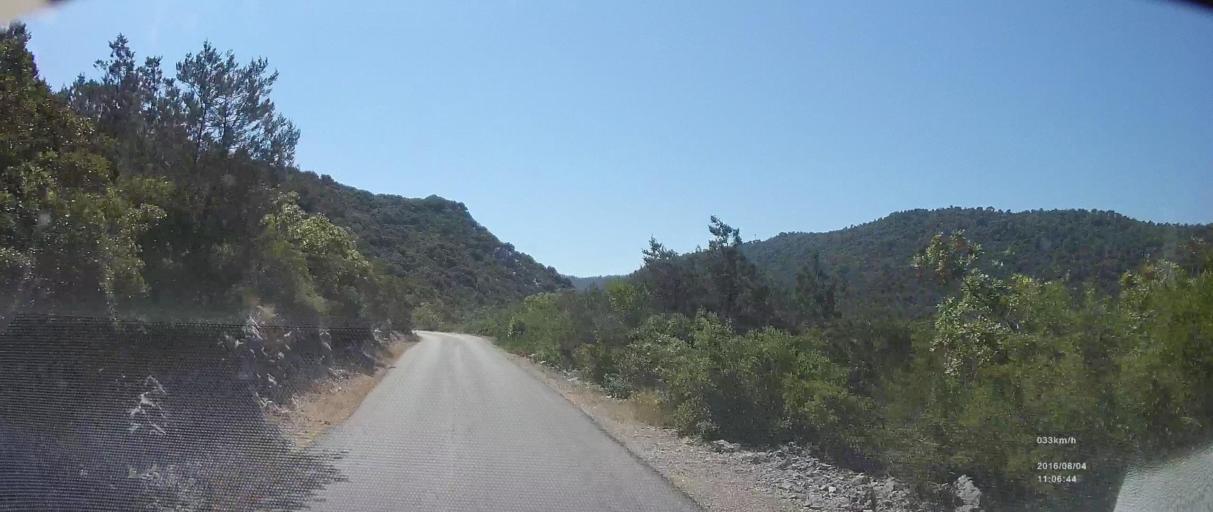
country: HR
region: Dubrovacko-Neretvanska
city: Blato
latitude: 42.7710
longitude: 17.4655
